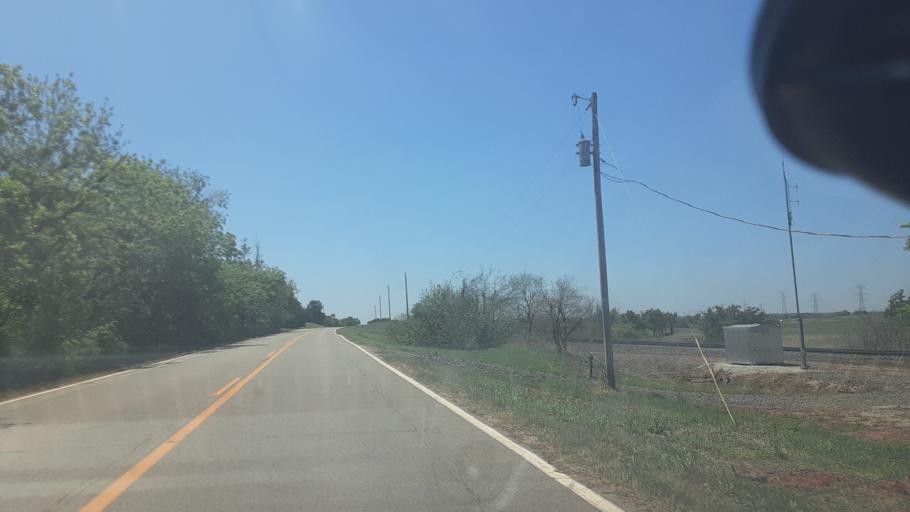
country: US
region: Oklahoma
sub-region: Logan County
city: Langston
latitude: 36.0896
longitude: -97.3963
